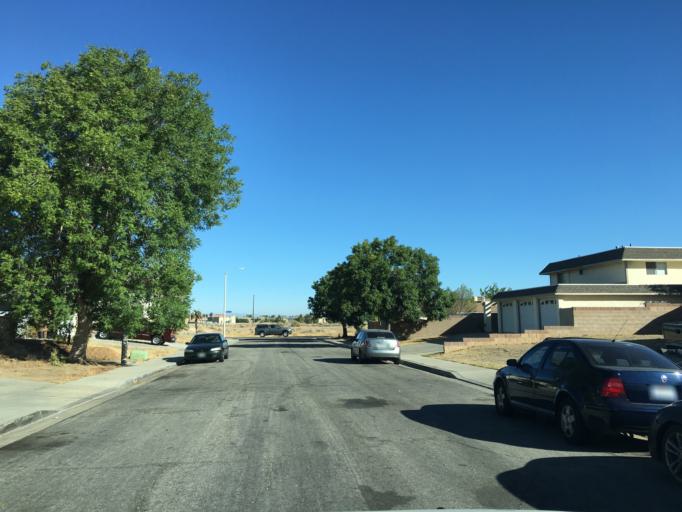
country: US
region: California
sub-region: Los Angeles County
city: Desert View Highlands
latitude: 34.5917
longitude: -118.1561
